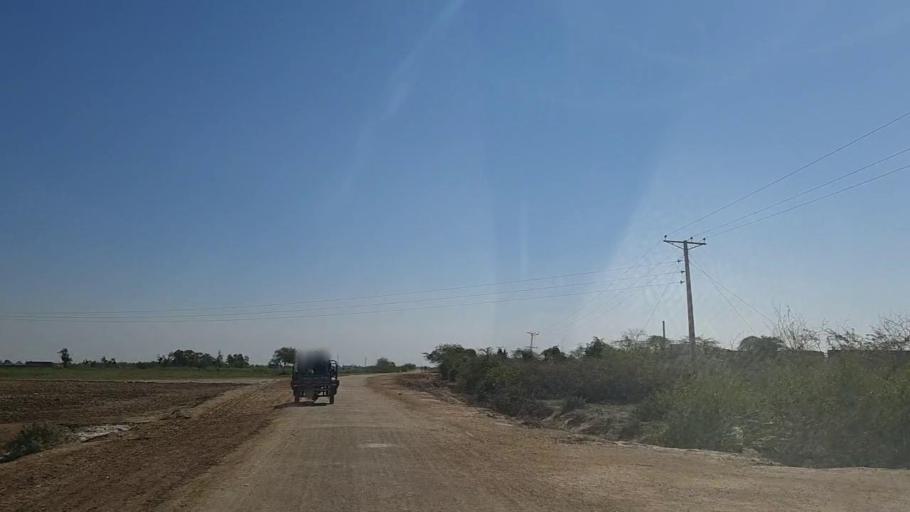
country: PK
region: Sindh
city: Samaro
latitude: 25.3100
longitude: 69.4763
